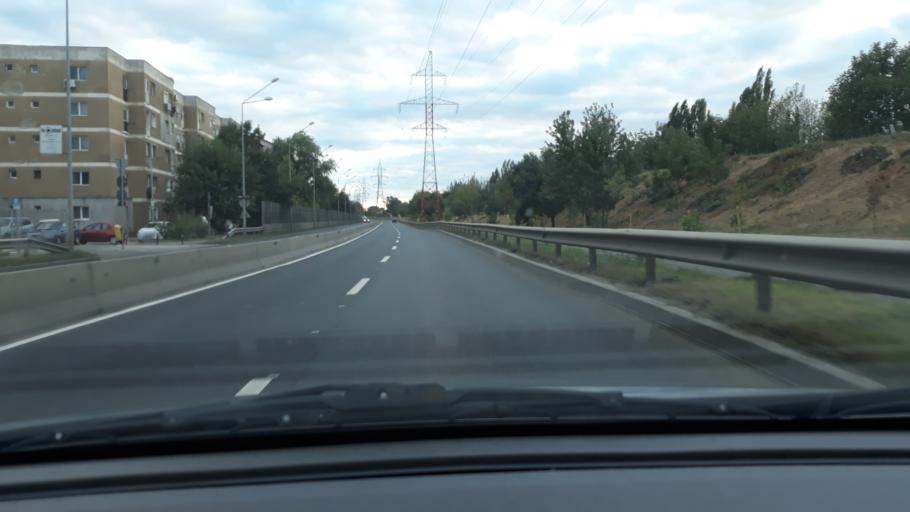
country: RO
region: Bihor
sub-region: Comuna Biharea
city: Oradea
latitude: 47.0789
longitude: 21.9102
